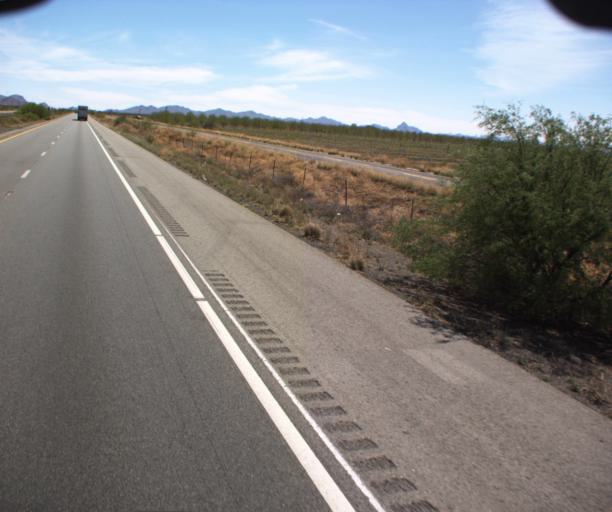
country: US
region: New Mexico
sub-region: Hidalgo County
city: Lordsburg
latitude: 32.2558
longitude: -109.1721
